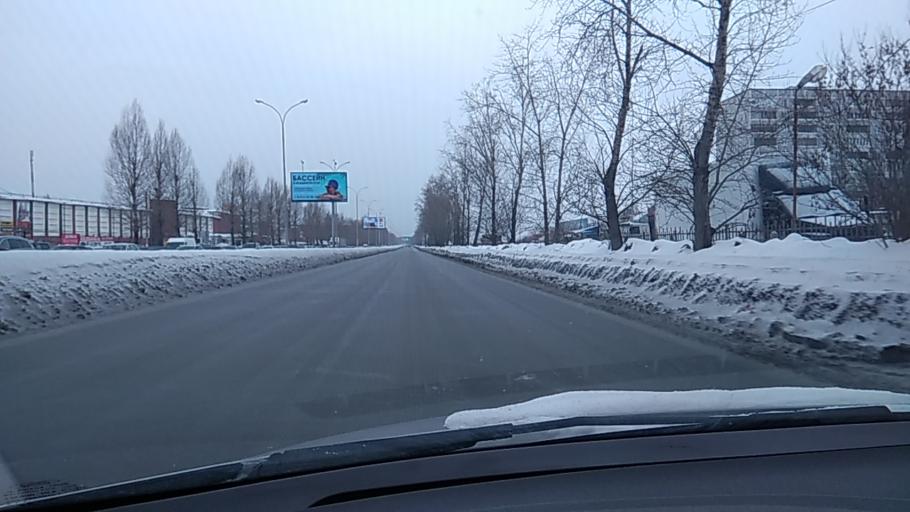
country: RU
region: Sverdlovsk
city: Sovkhoznyy
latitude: 56.7925
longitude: 60.5711
